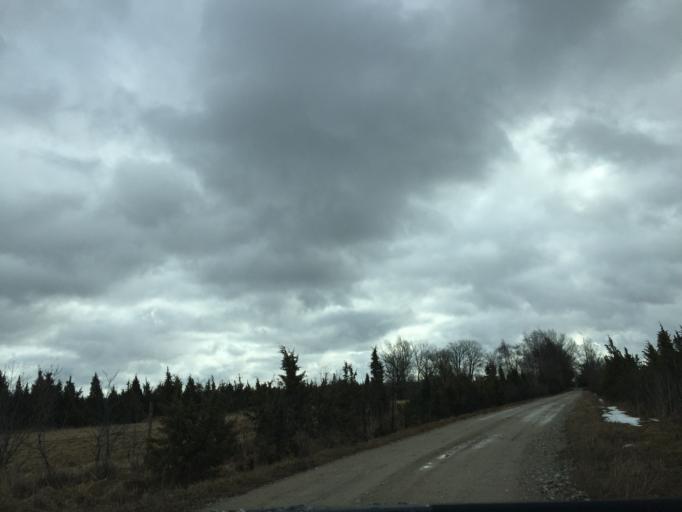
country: EE
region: Laeaene
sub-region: Haapsalu linn
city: Haapsalu
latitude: 58.6865
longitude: 23.5033
